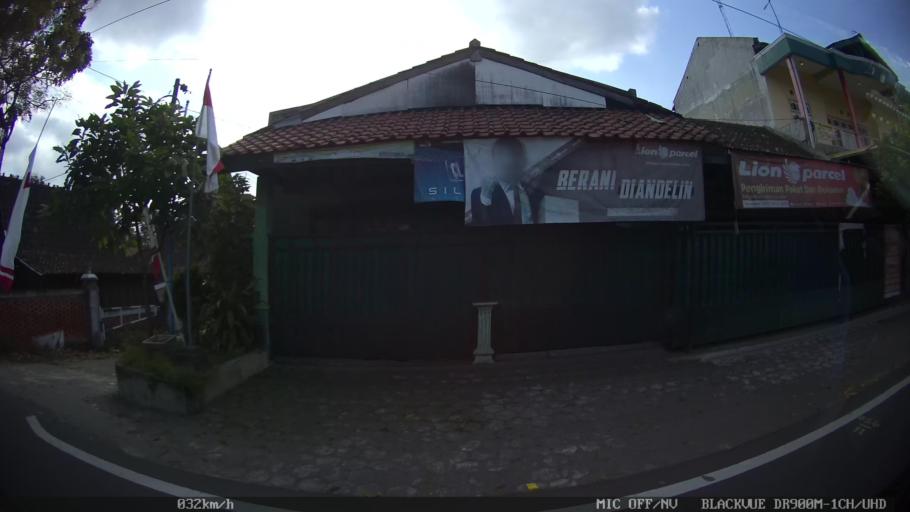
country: ID
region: Daerah Istimewa Yogyakarta
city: Kasihan
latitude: -7.8292
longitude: 110.3583
